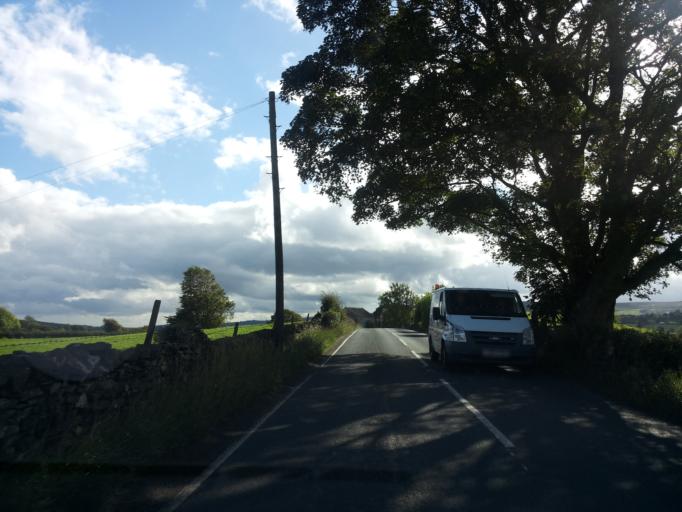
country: GB
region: England
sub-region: North Yorkshire
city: Leyburn
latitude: 54.3022
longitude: -1.8227
